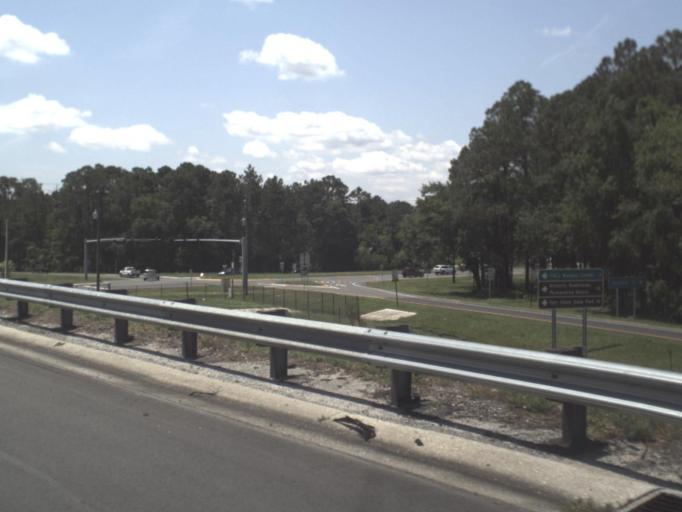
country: US
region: Florida
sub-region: Nassau County
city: Yulee
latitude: 30.6205
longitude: -81.6505
